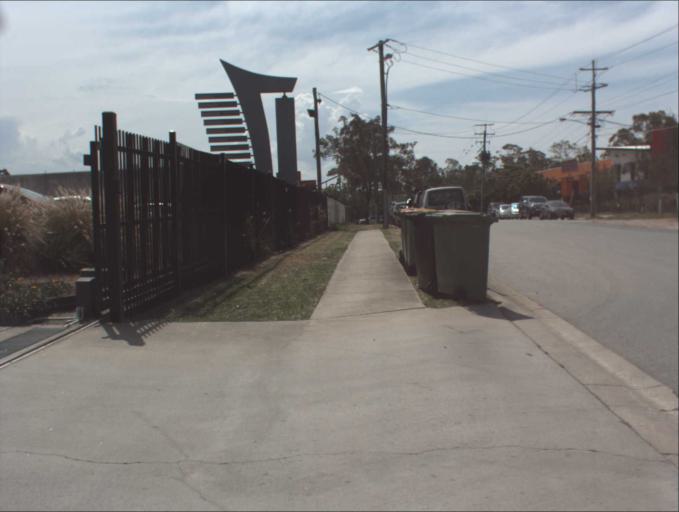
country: AU
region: Queensland
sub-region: Logan
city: Beenleigh
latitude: -27.6760
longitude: 153.1882
